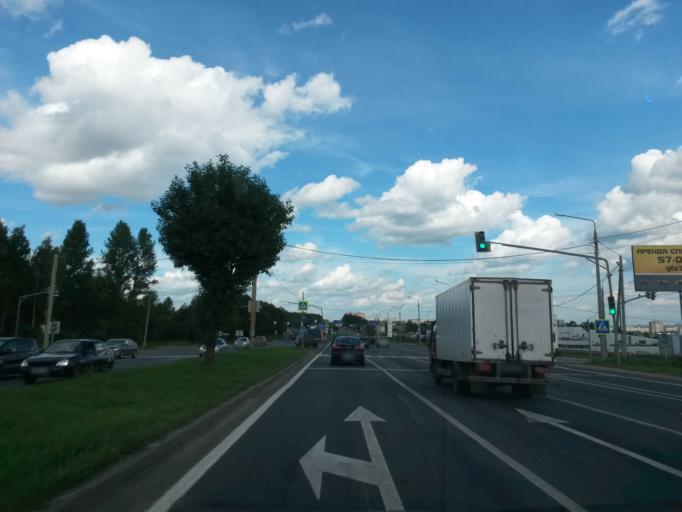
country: RU
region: Jaroslavl
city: Yaroslavl
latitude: 57.5607
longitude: 39.8236
